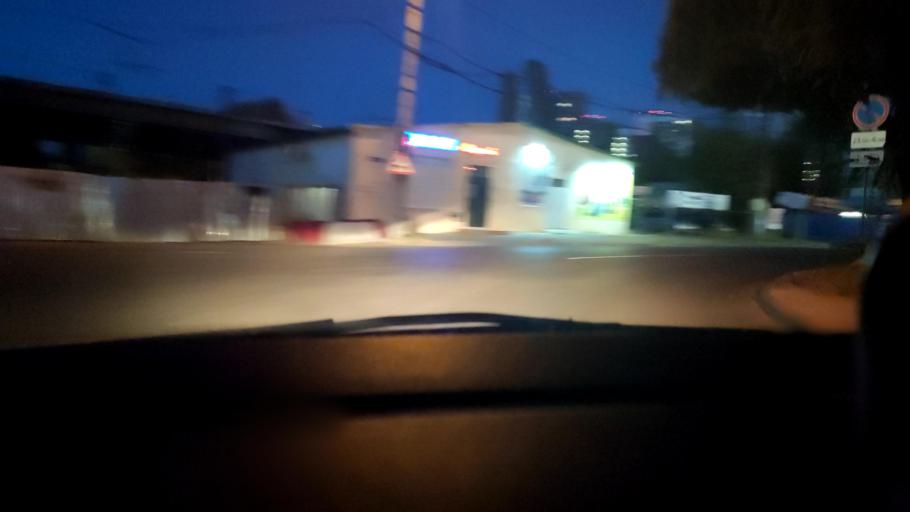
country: RU
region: Voronezj
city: Voronezh
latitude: 51.6672
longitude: 39.1702
